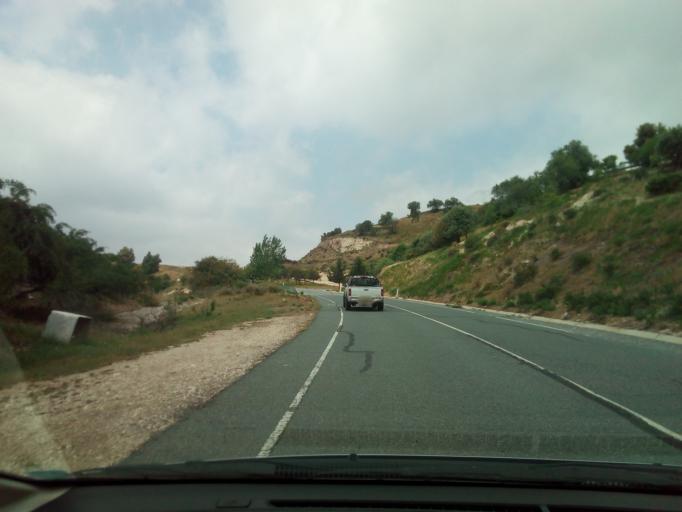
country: CY
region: Limassol
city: Pissouri
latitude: 34.8020
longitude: 32.6493
